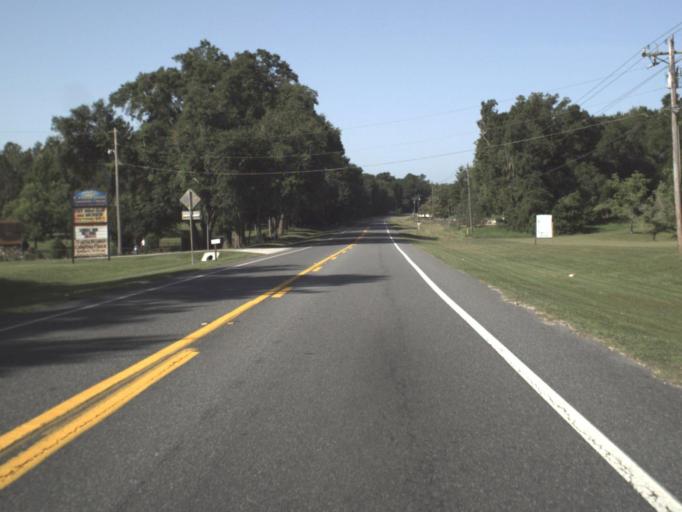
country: US
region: Florida
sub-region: Columbia County
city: Lake City
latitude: 30.1020
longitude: -82.6655
